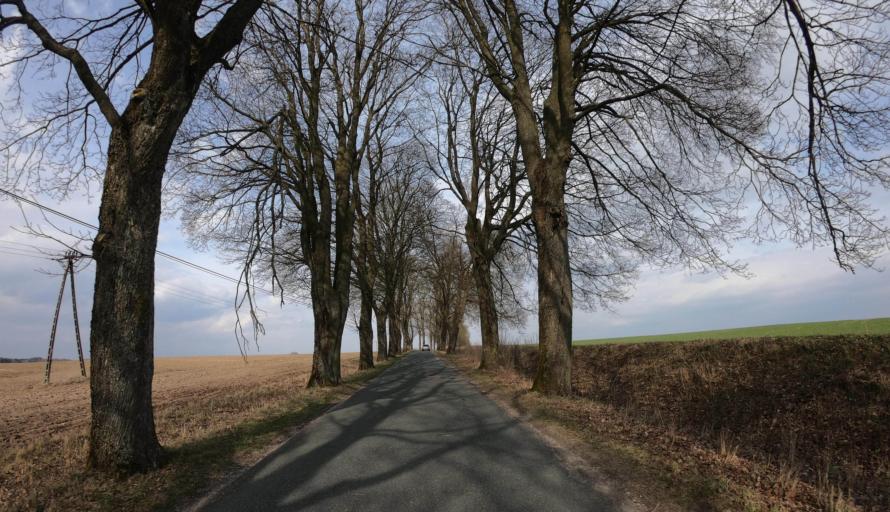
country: PL
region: West Pomeranian Voivodeship
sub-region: Powiat swidwinski
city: Swidwin
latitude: 53.8292
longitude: 15.8288
